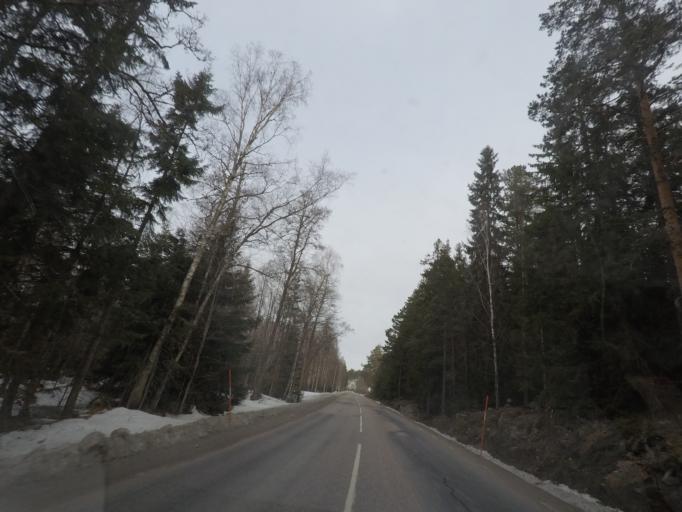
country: SE
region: Vaestmanland
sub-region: Vasteras
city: Skultuna
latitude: 59.7500
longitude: 16.3251
